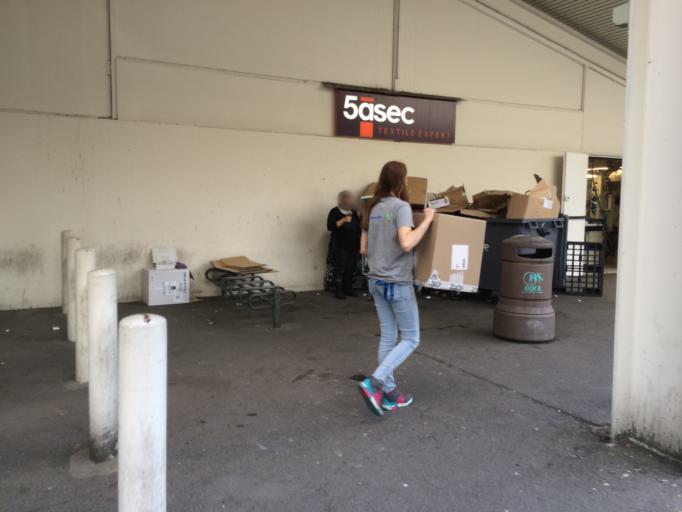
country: FR
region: Ile-de-France
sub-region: Departement de l'Essonne
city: Massy
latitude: 48.7250
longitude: 2.2779
